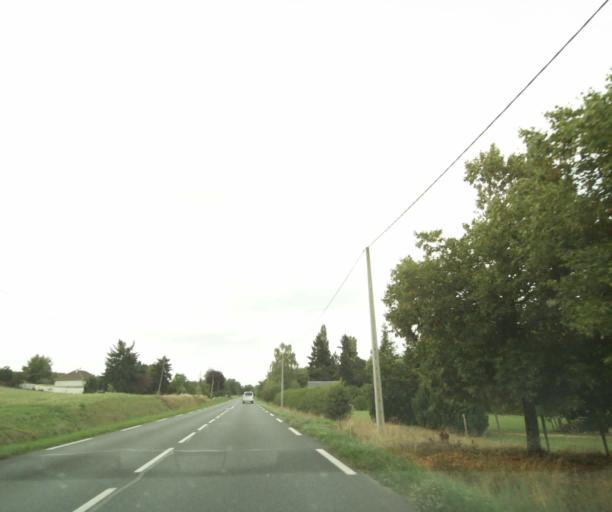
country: FR
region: Centre
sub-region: Departement d'Indre-et-Loire
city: Perrusson
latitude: 47.0616
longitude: 1.0825
